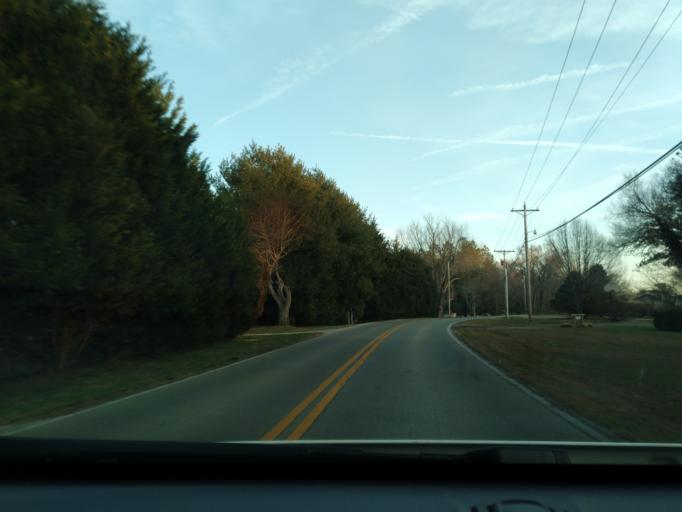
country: US
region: Maryland
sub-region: Calvert County
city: Huntingtown
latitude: 38.5990
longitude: -76.5664
